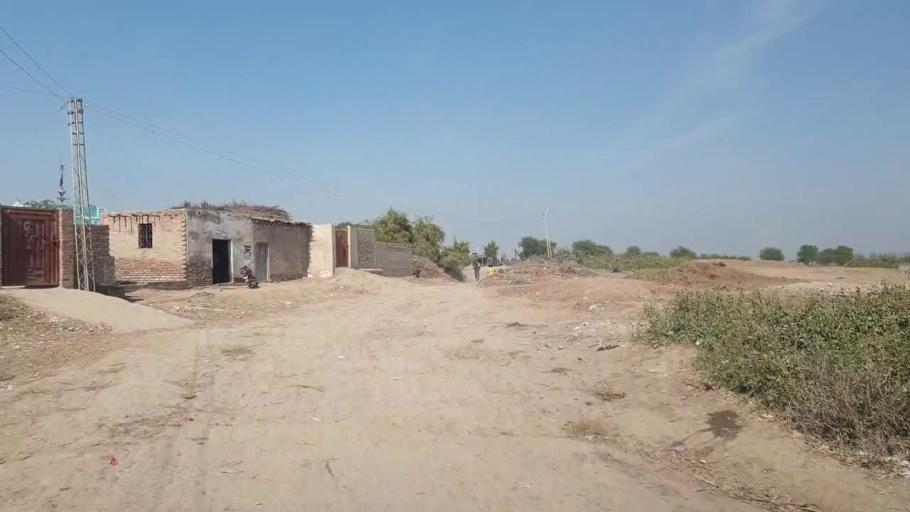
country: PK
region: Sindh
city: Chambar
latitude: 25.3279
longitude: 68.8268
